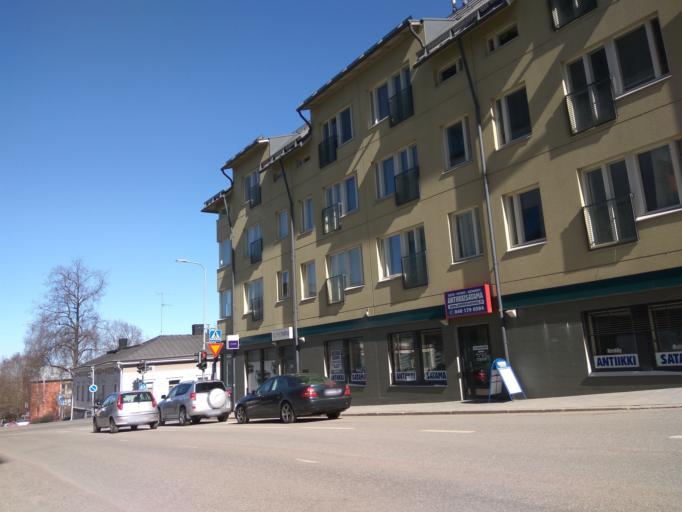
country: FI
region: South Karelia
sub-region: Lappeenranta
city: Lappeenranta
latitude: 61.0591
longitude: 28.1884
